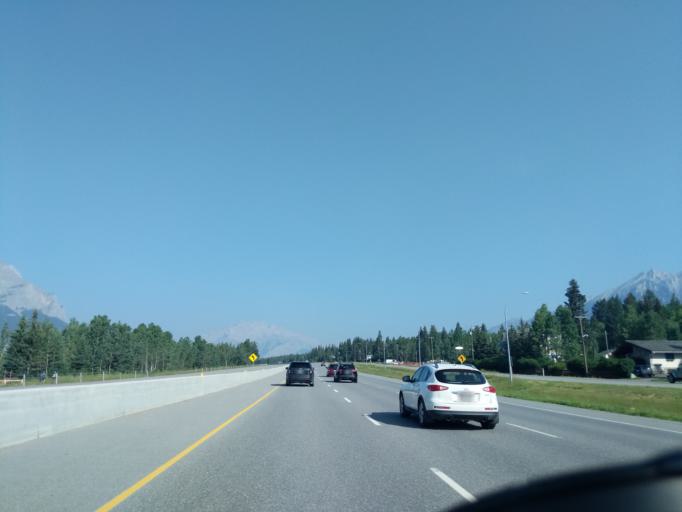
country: CA
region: Alberta
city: Canmore
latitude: 51.1225
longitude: -115.3840
